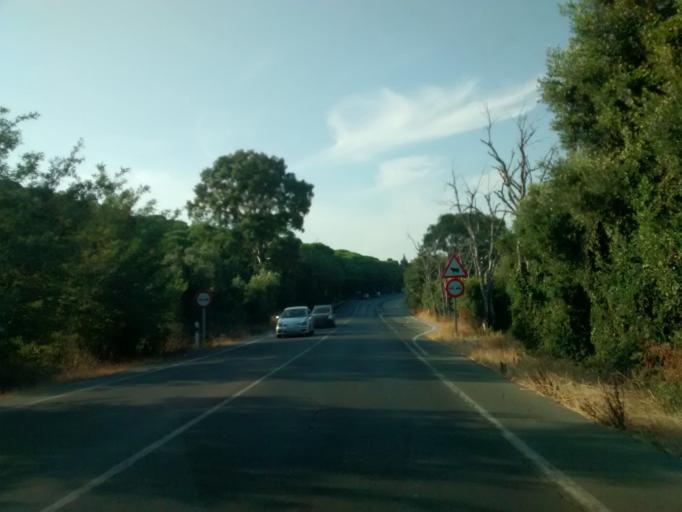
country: ES
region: Andalusia
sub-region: Provincia de Cadiz
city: Vejer de la Frontera
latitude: 36.2351
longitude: -5.9507
